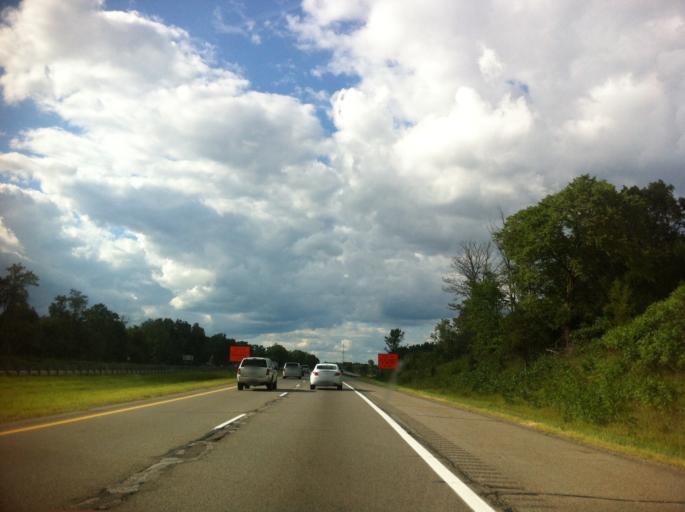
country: US
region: Michigan
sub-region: Livingston County
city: Whitmore Lake
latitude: 42.4564
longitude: -83.7527
